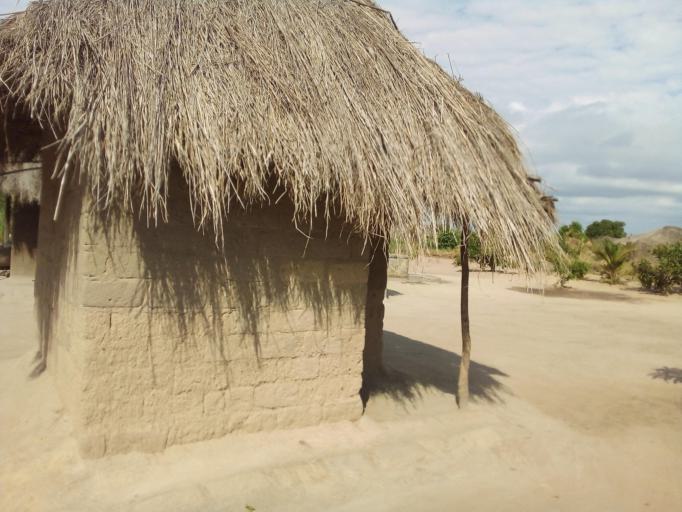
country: MZ
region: Zambezia
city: Quelimane
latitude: -17.5519
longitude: 36.7074
